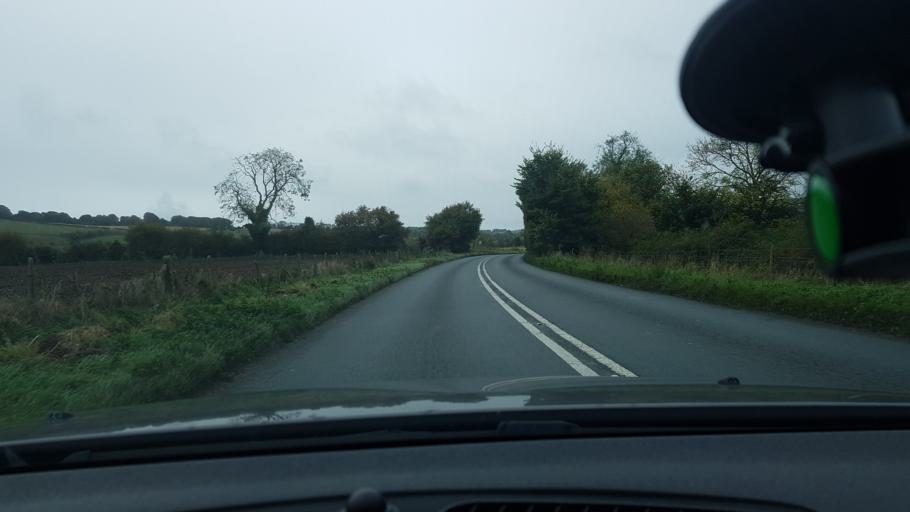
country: GB
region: England
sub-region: Wiltshire
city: Mildenhall
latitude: 51.4574
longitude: -1.7176
